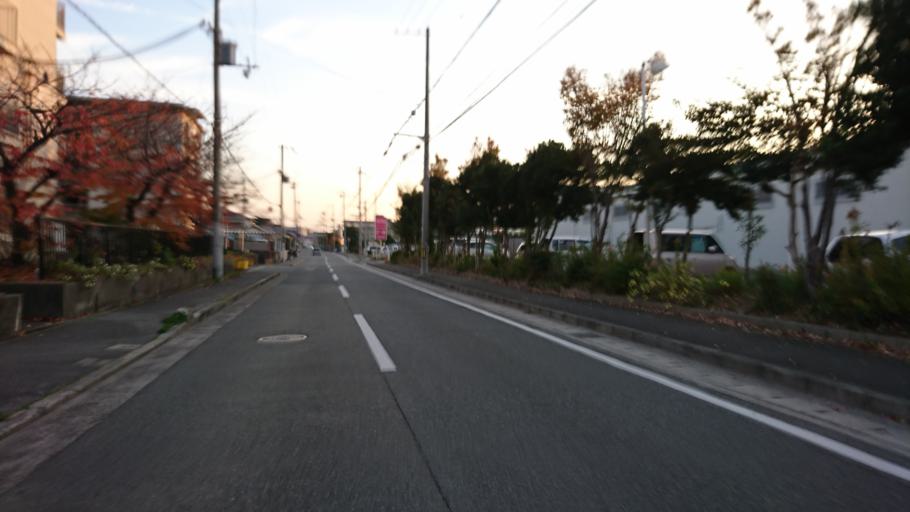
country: JP
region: Hyogo
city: Kakogawacho-honmachi
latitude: 34.7635
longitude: 134.8629
